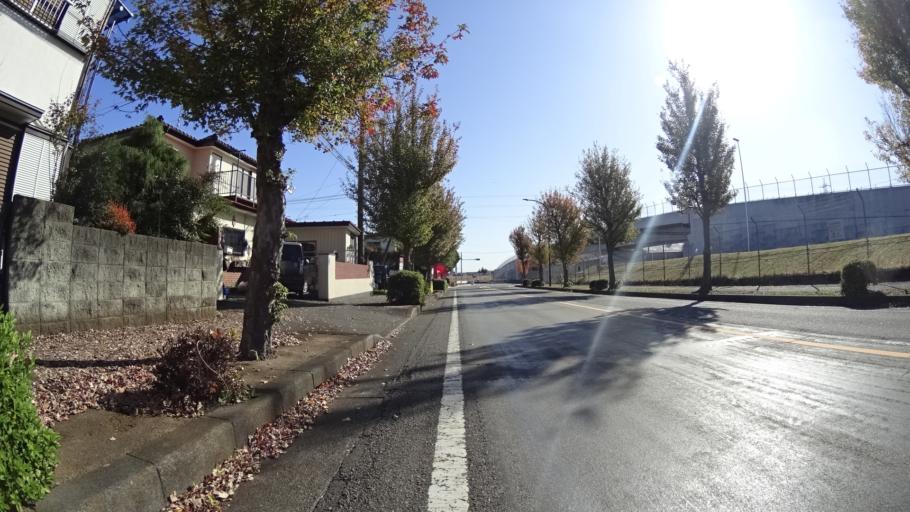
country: JP
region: Tokyo
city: Hachioji
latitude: 35.5886
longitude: 139.3764
